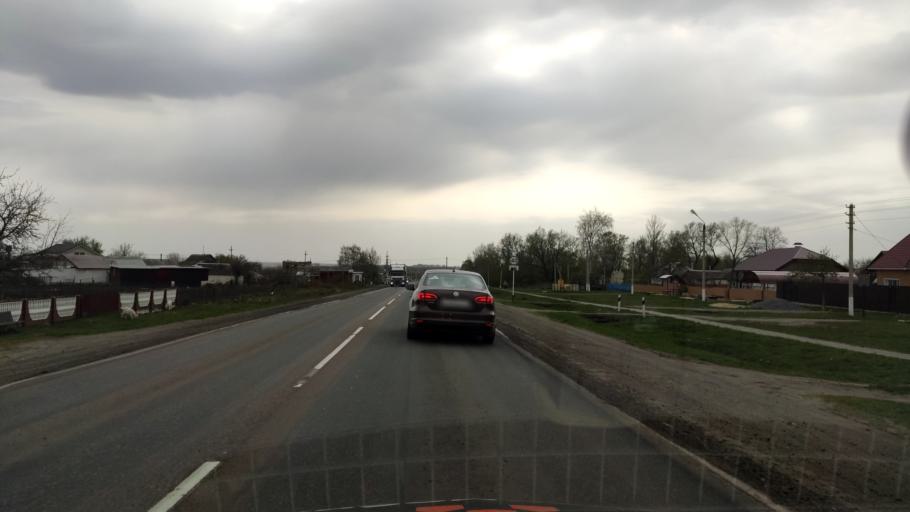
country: RU
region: Kursk
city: Gorshechnoye
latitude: 51.5202
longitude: 38.0182
